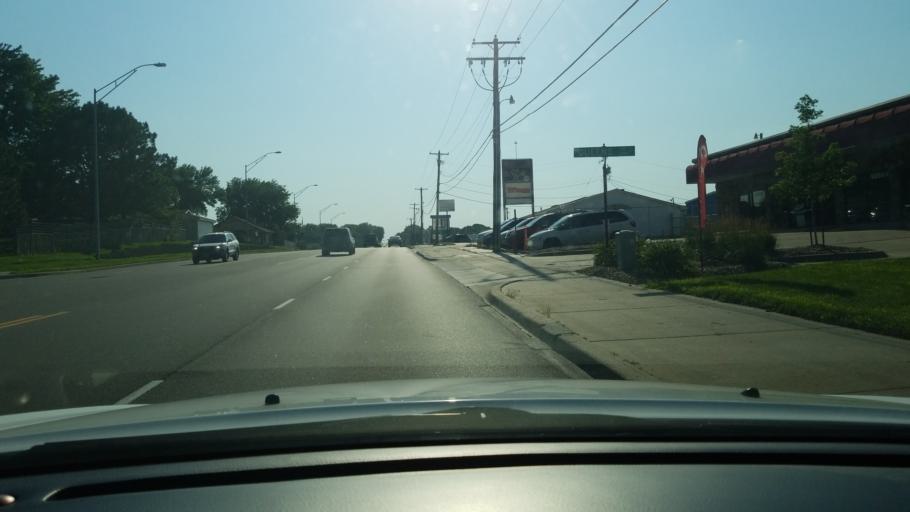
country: US
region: Nebraska
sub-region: Lancaster County
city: Lincoln
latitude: 40.7553
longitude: -96.6491
